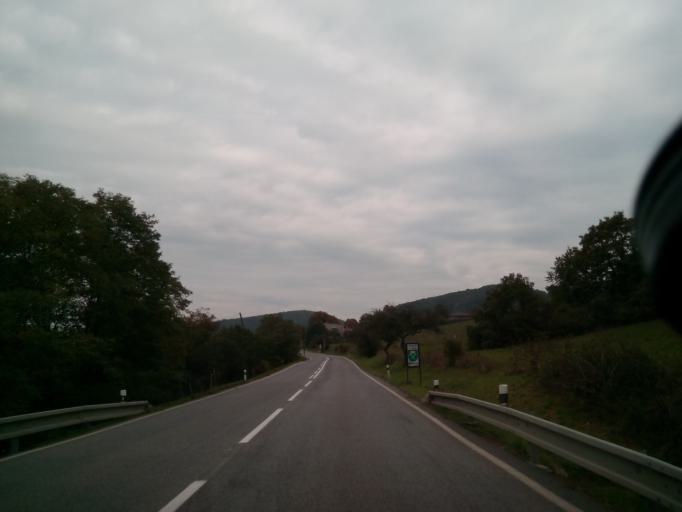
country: SK
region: Presovsky
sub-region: Okres Presov
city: Presov
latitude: 49.1022
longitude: 21.3151
